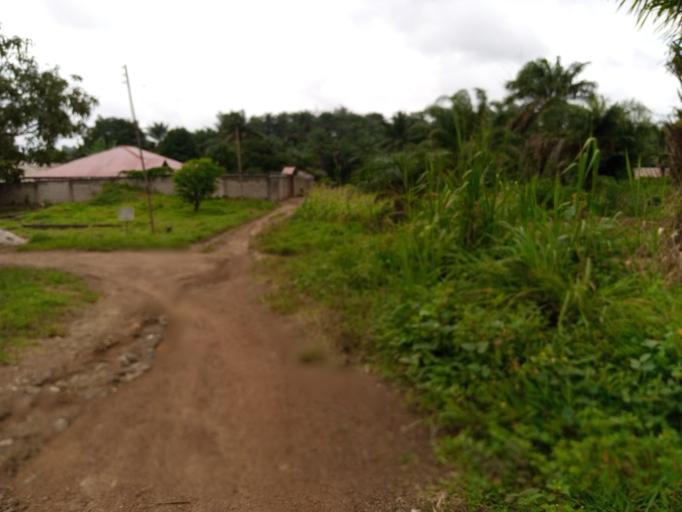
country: SL
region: Eastern Province
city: Kenema
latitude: 7.8793
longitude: -11.1729
